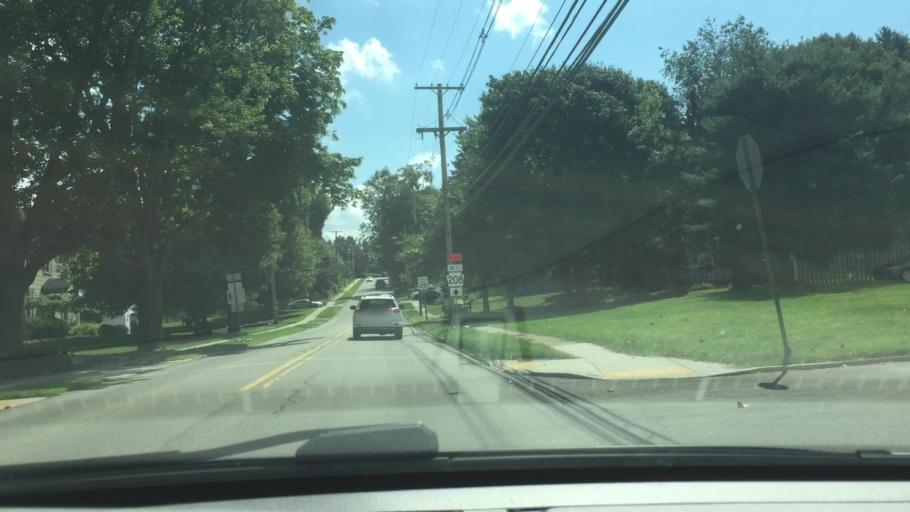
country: US
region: Pennsylvania
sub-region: Lawrence County
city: New Wilmington
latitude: 41.1176
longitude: -80.3354
